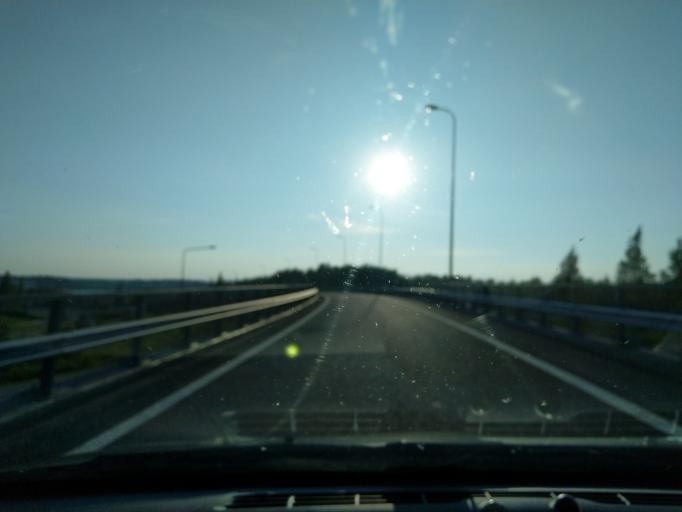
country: FI
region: Paijanne Tavastia
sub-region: Lahti
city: Lahti
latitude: 60.9702
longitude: 25.7240
